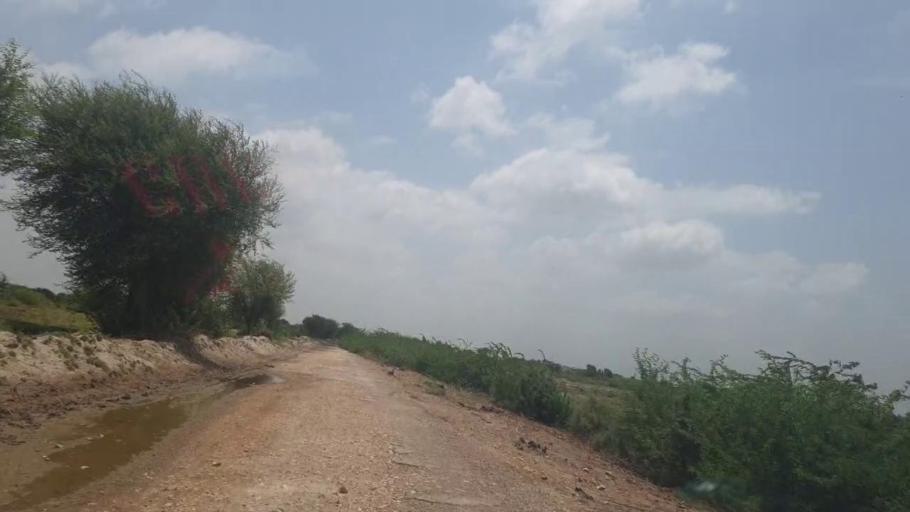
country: PK
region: Sindh
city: Tando Mittha Khan
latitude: 25.9164
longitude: 69.2318
